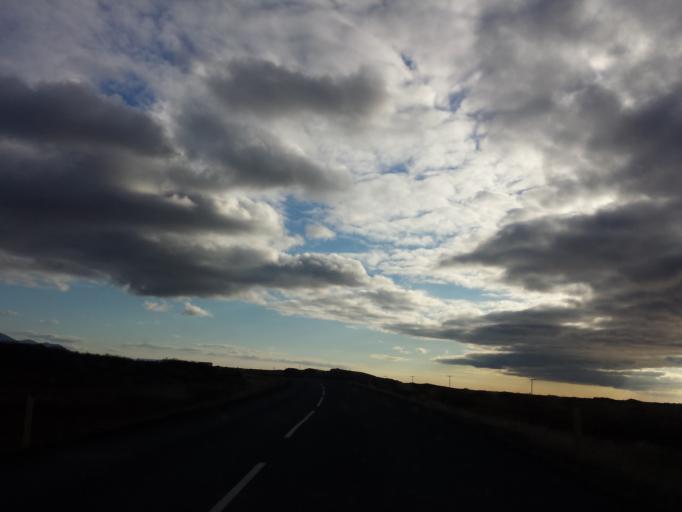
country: IS
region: West
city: Borgarnes
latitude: 64.6405
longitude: -22.0682
